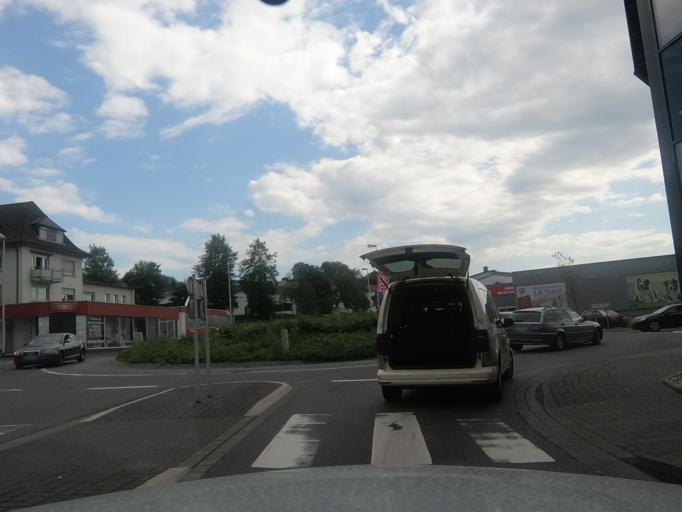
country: DE
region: North Rhine-Westphalia
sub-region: Regierungsbezirk Arnsberg
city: Olpe
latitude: 51.0237
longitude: 7.8444
